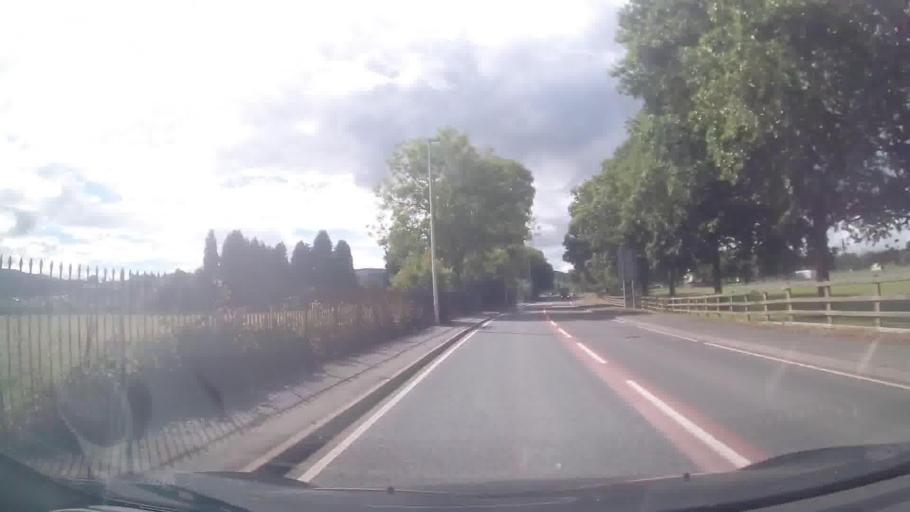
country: GB
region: Wales
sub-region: Sir Powys
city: Builth Wells
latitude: 52.1544
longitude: -3.3986
